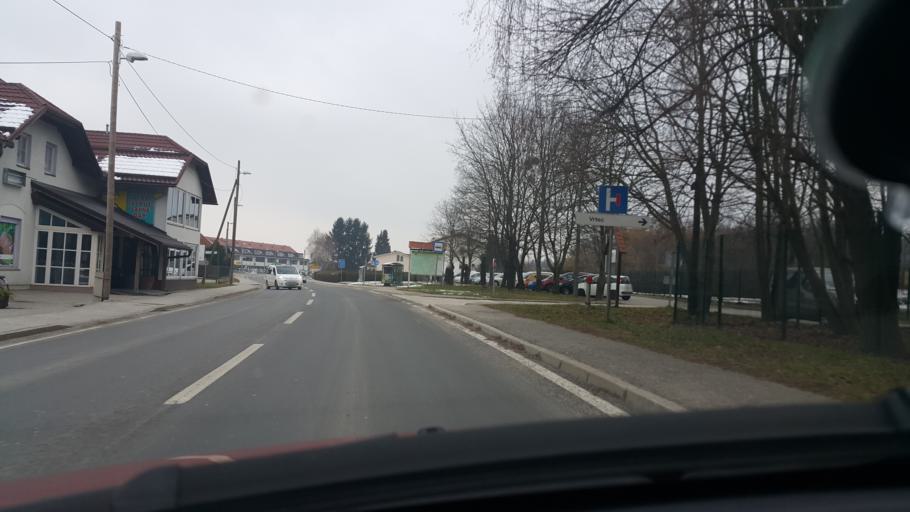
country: SI
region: Hoce-Slivnica
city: Radizel
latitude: 46.4778
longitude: 15.6537
